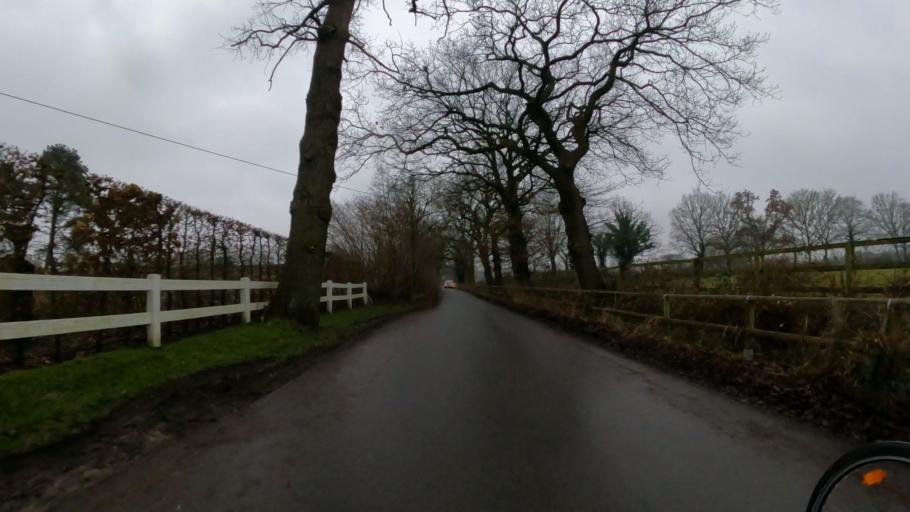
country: DE
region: Schleswig-Holstein
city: Rellingen
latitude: 53.5904
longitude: 9.7895
